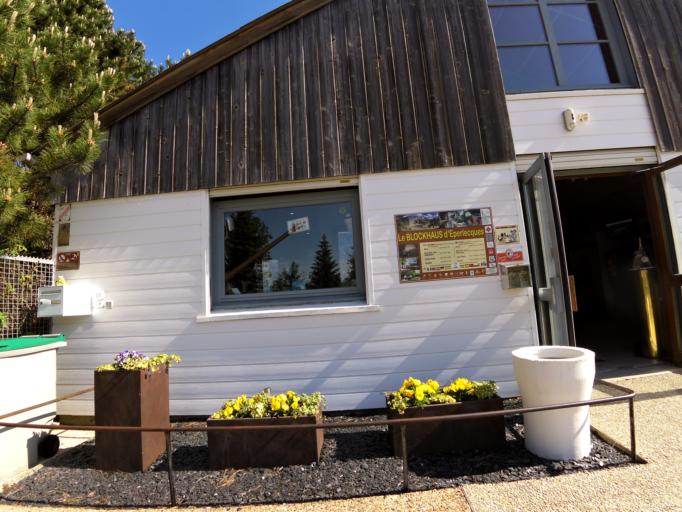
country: FR
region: Nord-Pas-de-Calais
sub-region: Departement du Nord
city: Watten
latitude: 50.8272
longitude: 2.1822
